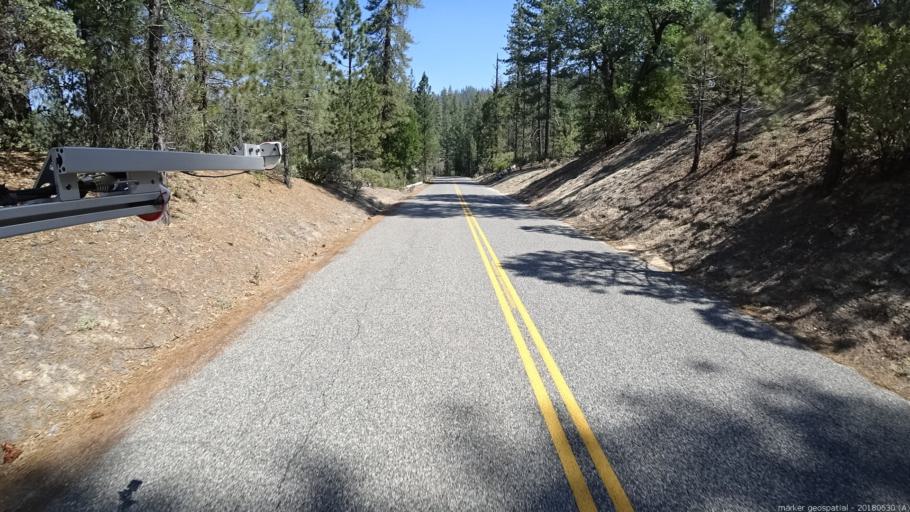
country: US
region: California
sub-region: Madera County
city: Oakhurst
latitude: 37.3796
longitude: -119.3808
